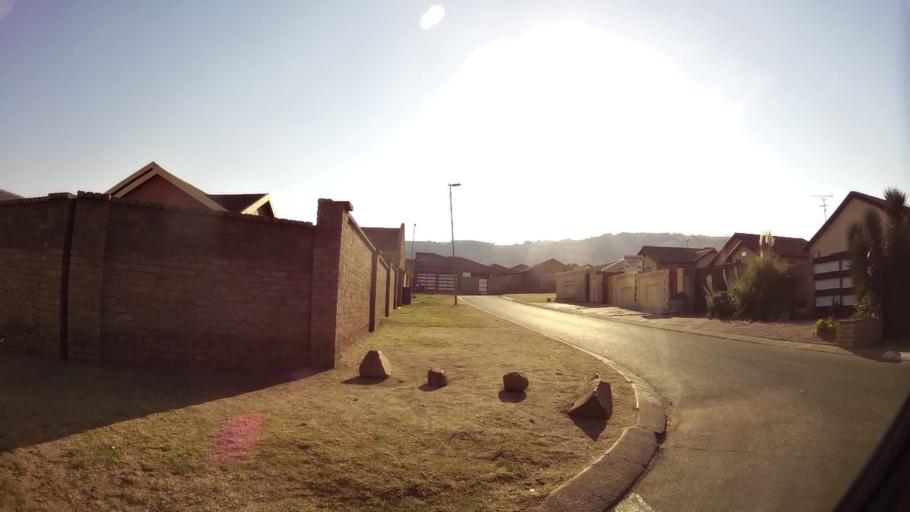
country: ZA
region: Gauteng
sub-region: City of Johannesburg Metropolitan Municipality
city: Soweto
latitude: -26.2965
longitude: 27.9605
